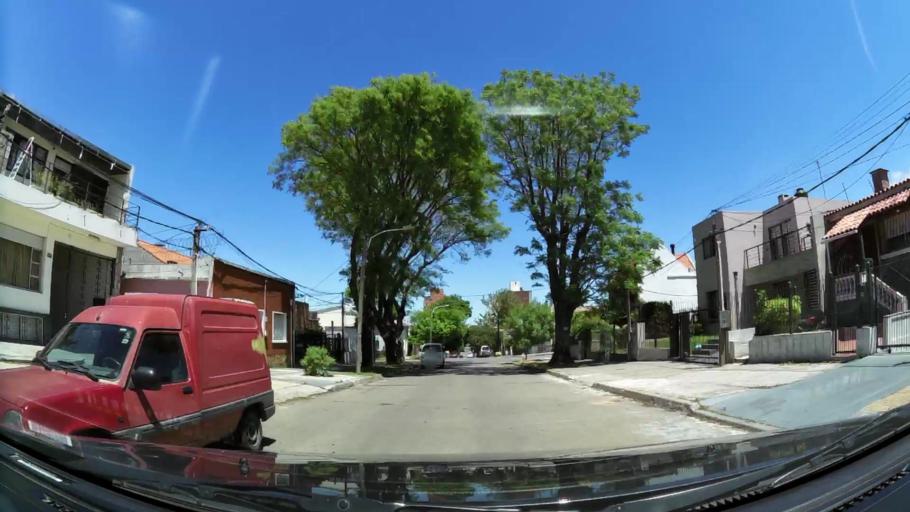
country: UY
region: Montevideo
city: Montevideo
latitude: -34.8918
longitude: -56.1439
